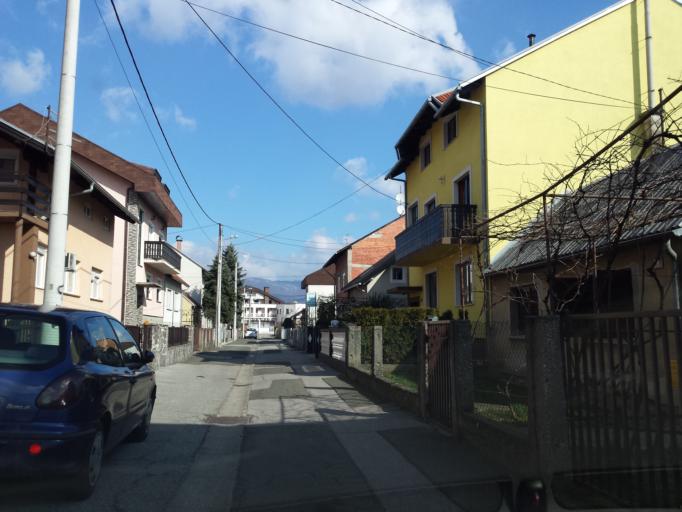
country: HR
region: Grad Zagreb
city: Jankomir
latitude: 45.7997
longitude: 15.9160
